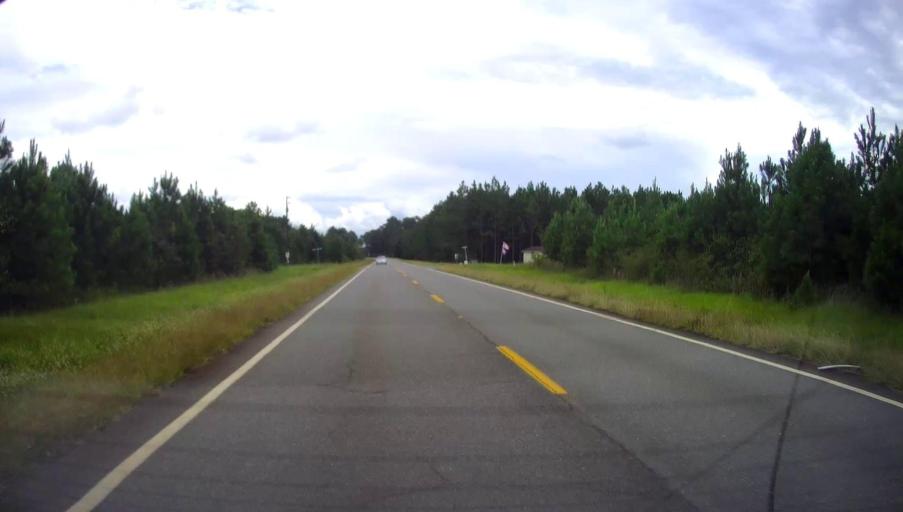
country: US
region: Georgia
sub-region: Marion County
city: Buena Vista
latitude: 32.2694
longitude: -84.4315
